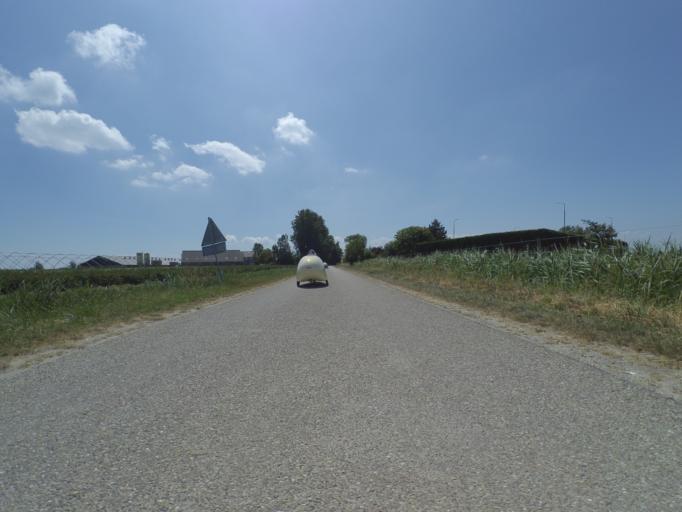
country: NL
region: Zeeland
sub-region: Gemeente Reimerswaal
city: Yerseke
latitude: 51.5772
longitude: 4.0071
